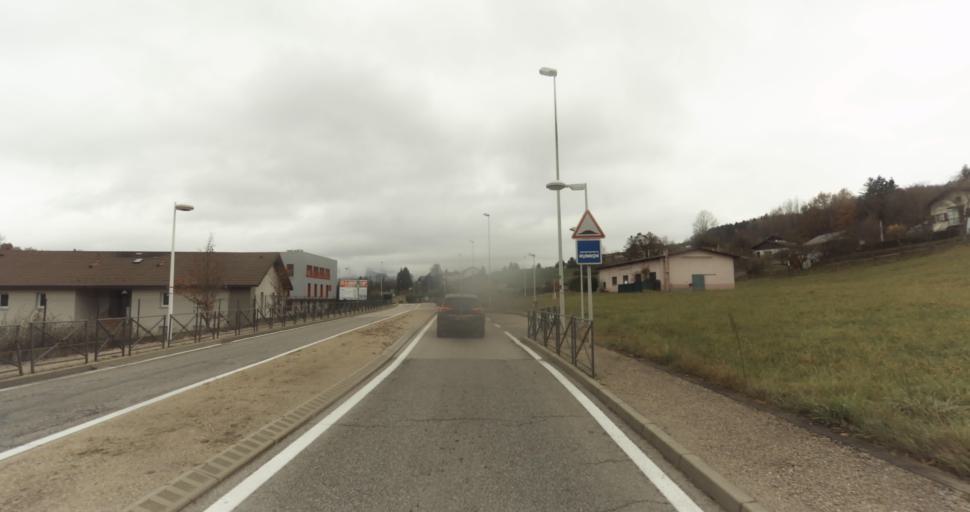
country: FR
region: Rhone-Alpes
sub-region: Departement de la Haute-Savoie
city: Saint-Martin-Bellevue
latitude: 45.9691
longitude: 6.1638
